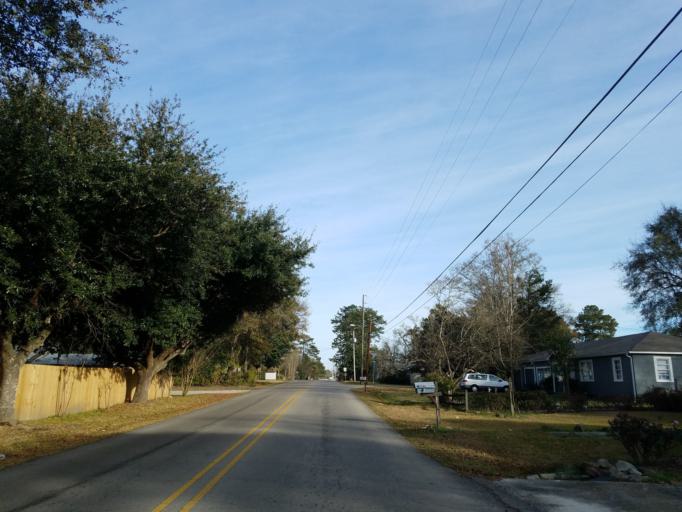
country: US
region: Mississippi
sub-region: Forrest County
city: Hattiesburg
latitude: 31.3174
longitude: -89.3119
